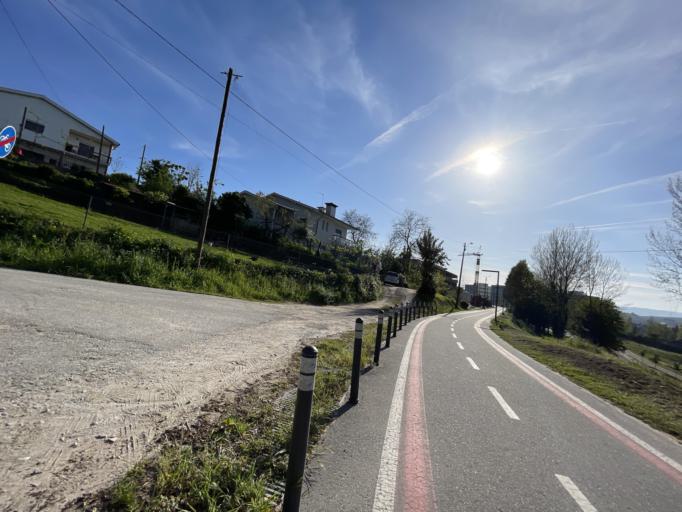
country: PT
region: Braga
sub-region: Guimaraes
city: Guimaraes
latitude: 41.4396
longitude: -8.2835
